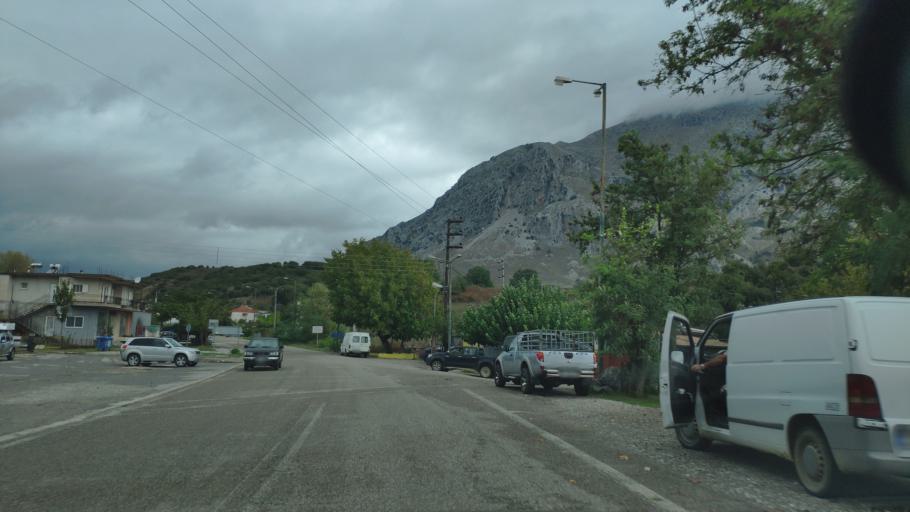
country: GR
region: West Greece
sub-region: Nomos Aitolias kai Akarnanias
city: Krikellos
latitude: 38.9726
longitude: 21.3309
